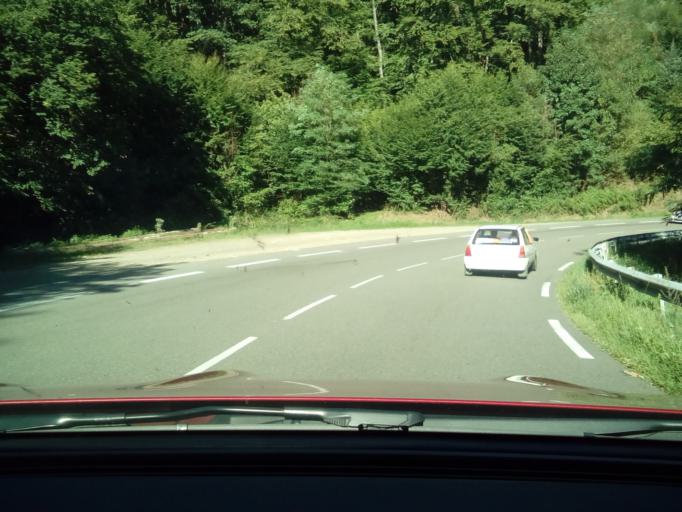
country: FR
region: Rhone-Alpes
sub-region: Departement du Rhone
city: Cublize
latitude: 45.9714
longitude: 4.4082
